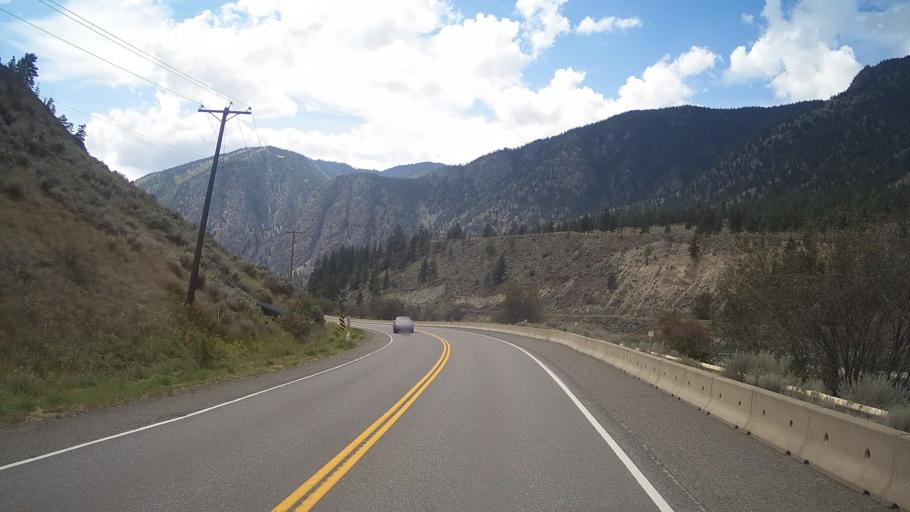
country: CA
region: British Columbia
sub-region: Thompson-Nicola Regional District
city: Ashcroft
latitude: 50.4019
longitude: -121.3780
